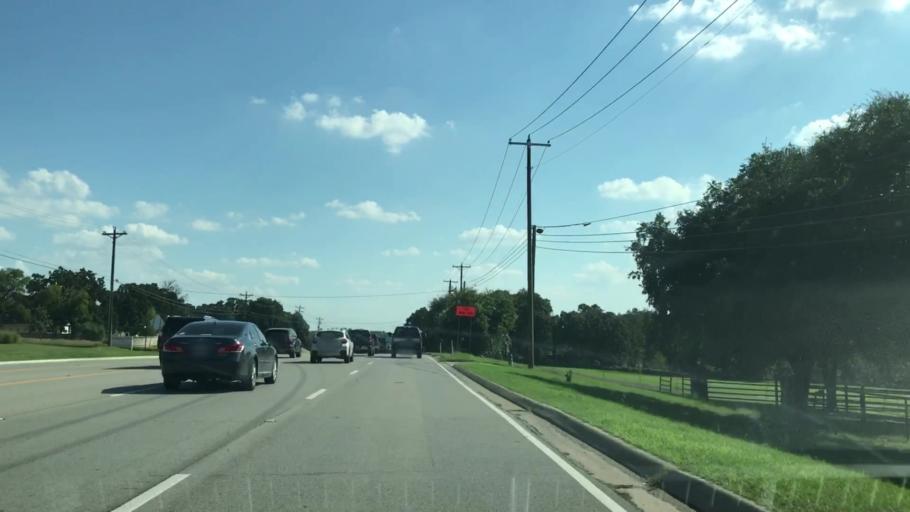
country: US
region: Texas
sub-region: Tarrant County
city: Southlake
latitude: 32.9325
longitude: -97.1859
